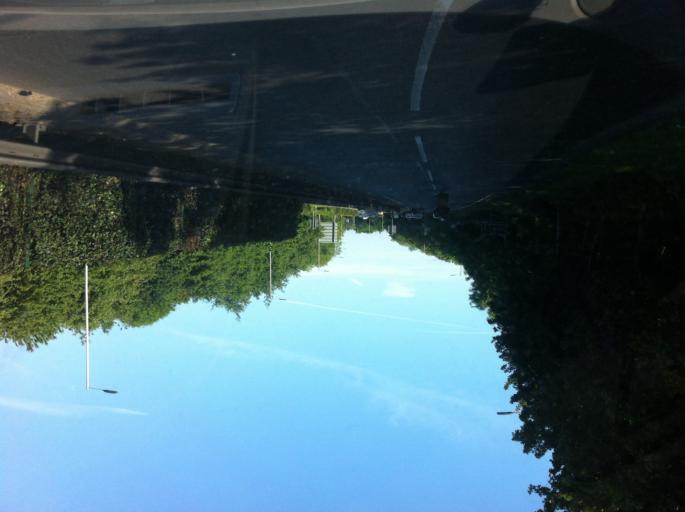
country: GB
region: England
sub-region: Greater London
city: Southall
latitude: 51.5249
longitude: -0.3914
